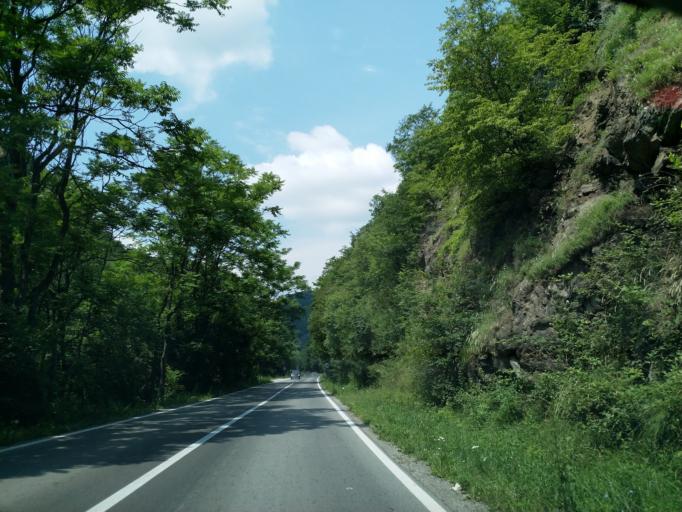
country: RS
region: Central Serbia
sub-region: Toplicki Okrug
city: Blace
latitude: 43.3342
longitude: 21.2068
